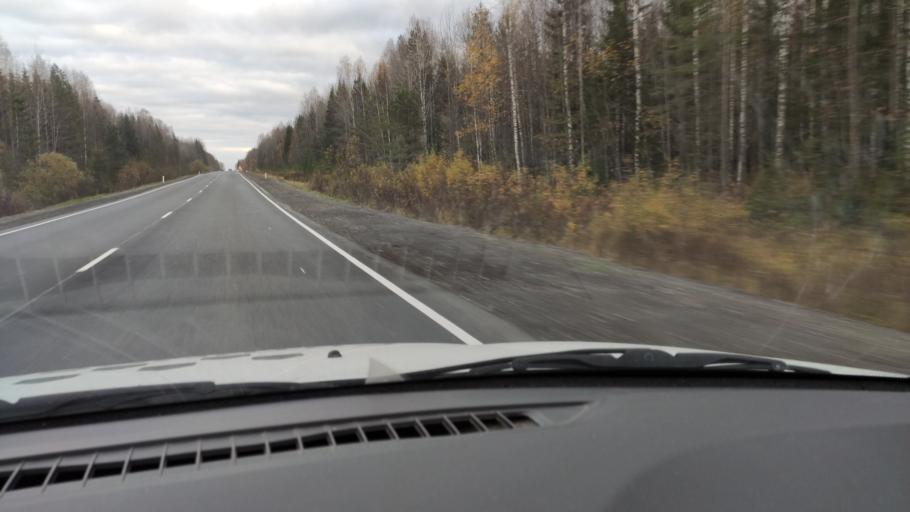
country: RU
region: Kirov
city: Chernaya Kholunitsa
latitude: 58.8803
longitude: 51.4418
